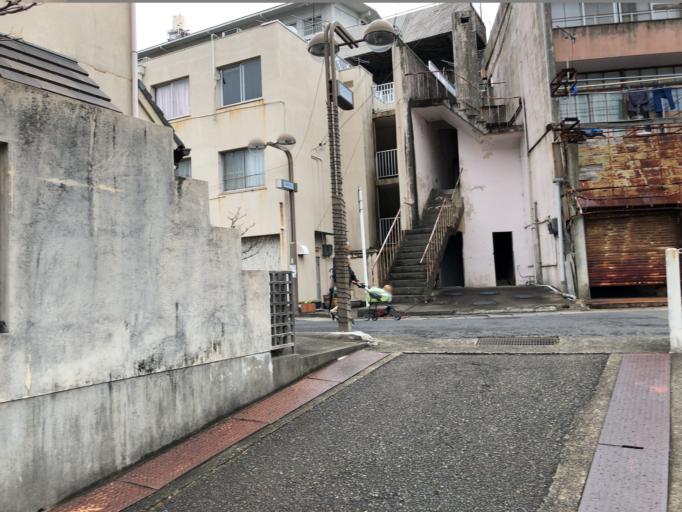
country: JP
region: Wakayama
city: Tanabe
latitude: 33.6828
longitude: 135.3473
